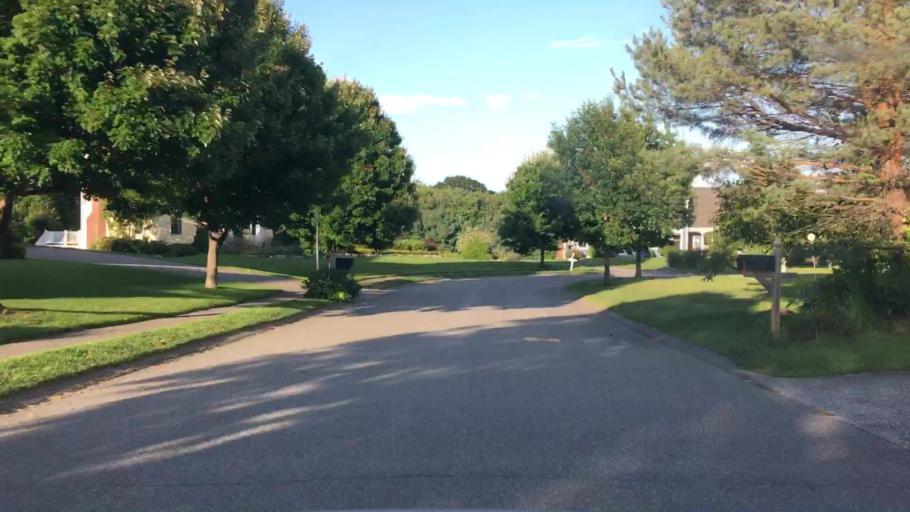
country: US
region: Maine
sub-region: Cumberland County
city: Scarborough
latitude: 43.5894
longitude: -70.2912
